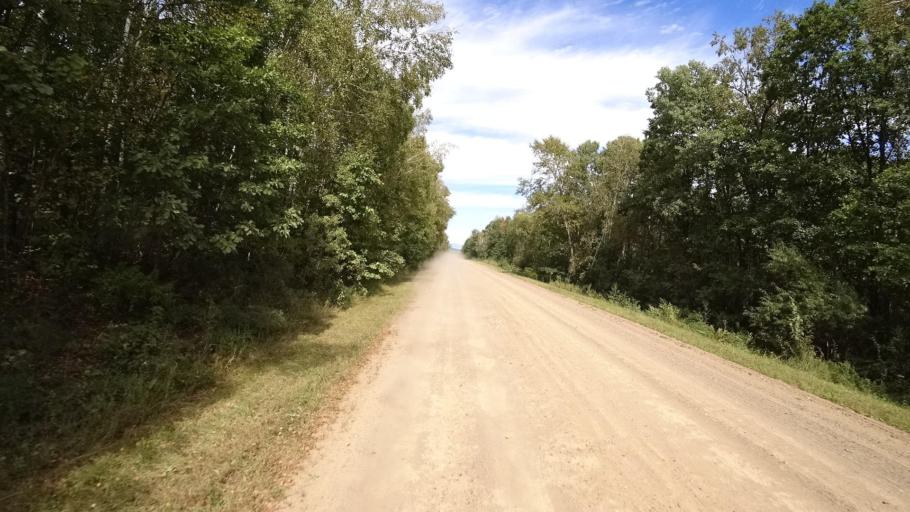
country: RU
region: Primorskiy
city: Yakovlevka
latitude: 44.6706
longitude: 133.6112
